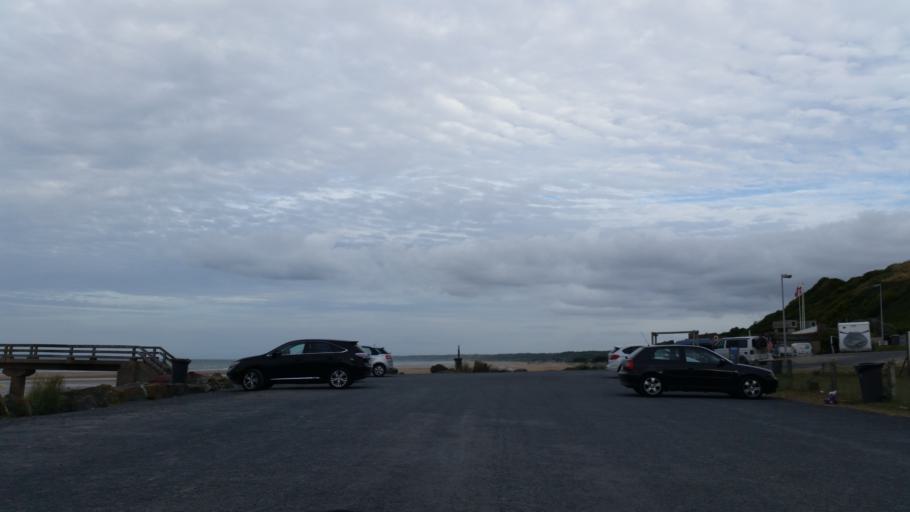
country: FR
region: Lower Normandy
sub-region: Departement du Calvados
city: Grandcamp-Maisy
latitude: 49.3803
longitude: -0.9044
